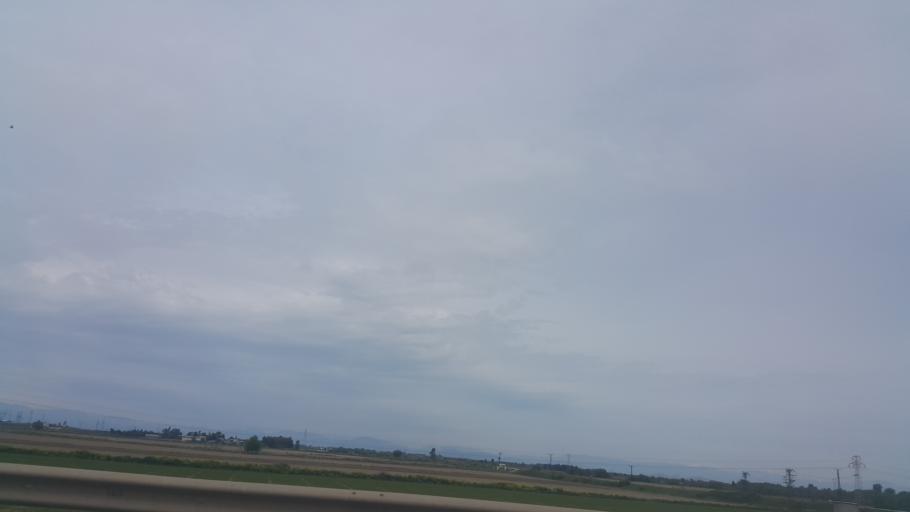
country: TR
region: Adana
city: Ceyhan
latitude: 37.0529
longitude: 35.7991
